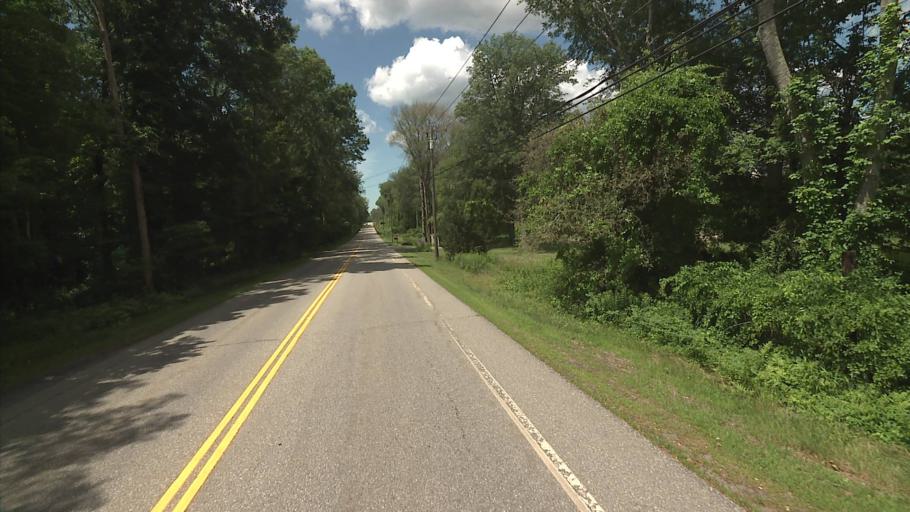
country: US
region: Connecticut
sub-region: New London County
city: Old Mystic
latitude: 41.4170
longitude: -71.9029
